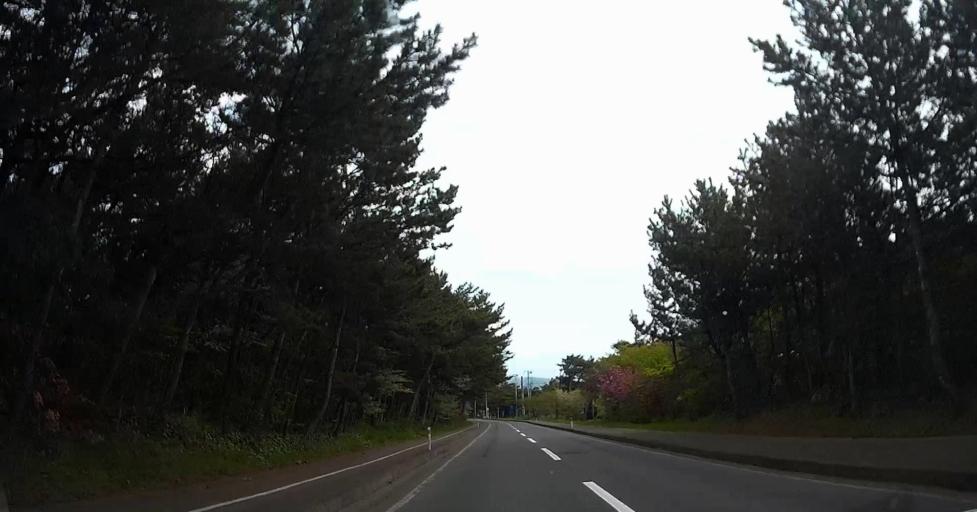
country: JP
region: Aomori
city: Shimokizukuri
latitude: 41.0420
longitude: 140.3263
